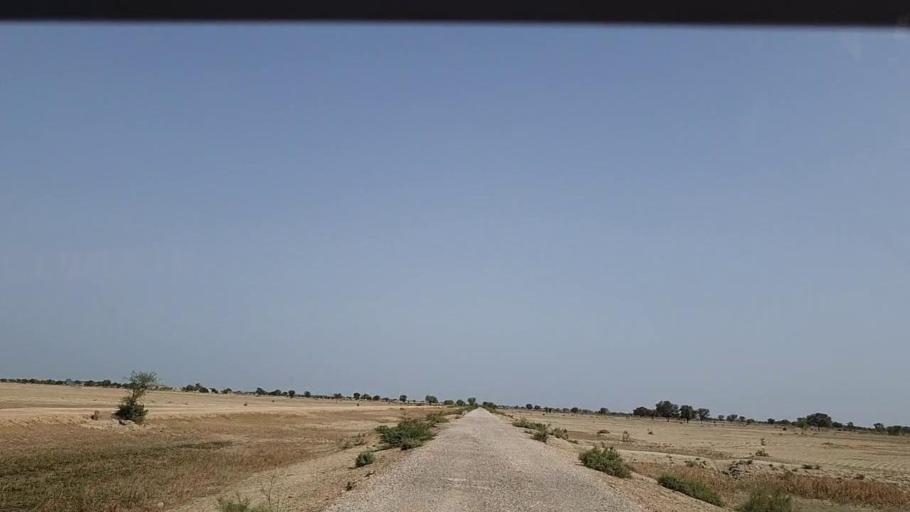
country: PK
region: Sindh
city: Johi
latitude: 26.7569
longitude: 67.6665
